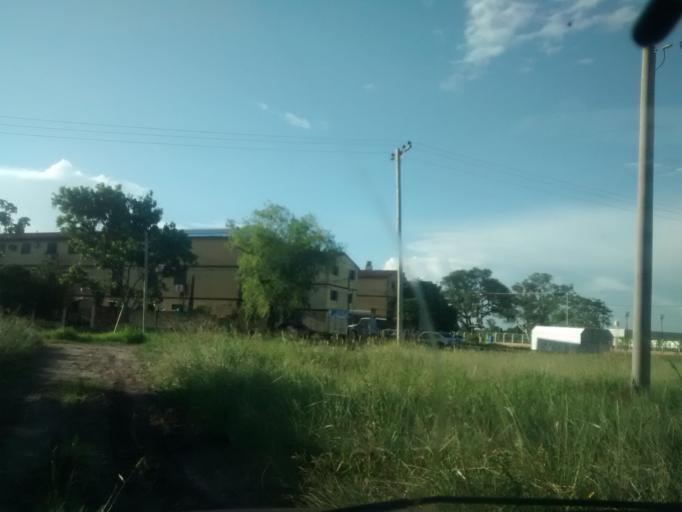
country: AR
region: Chaco
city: Fontana
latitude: -27.4464
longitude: -59.0123
